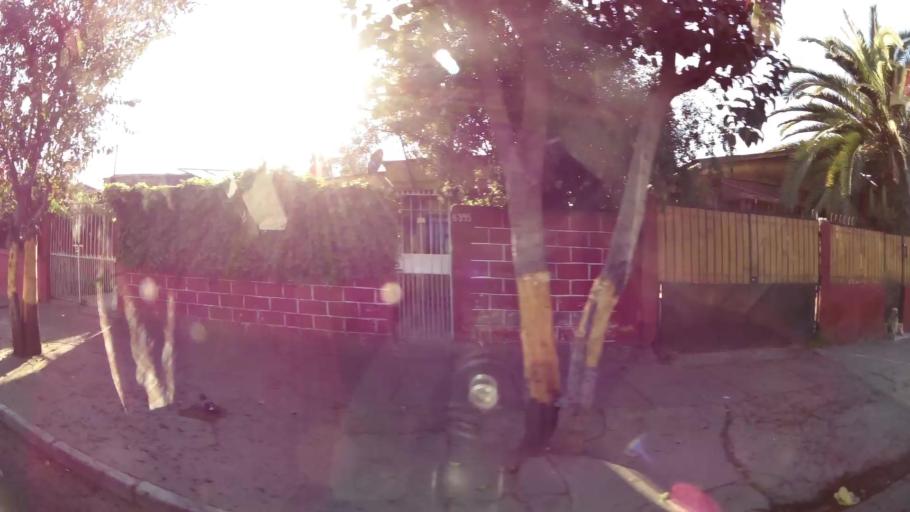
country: CL
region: Santiago Metropolitan
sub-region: Provincia de Santiago
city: Santiago
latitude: -33.3776
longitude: -70.6718
